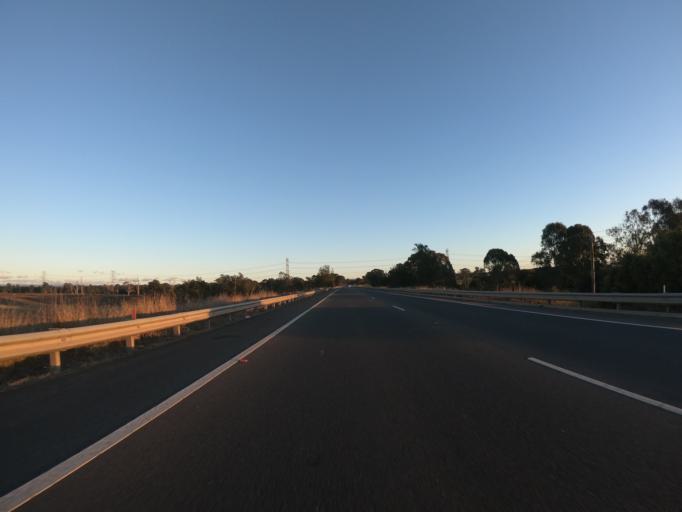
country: AU
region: New South Wales
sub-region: Blacktown
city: Riverstone
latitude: -33.6793
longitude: 150.8142
